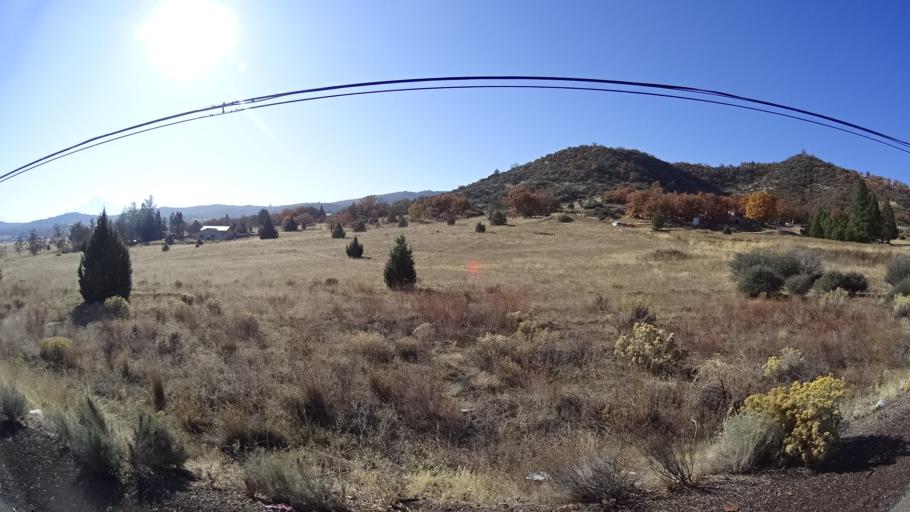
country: US
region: California
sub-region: Siskiyou County
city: Yreka
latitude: 41.7120
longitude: -122.6107
